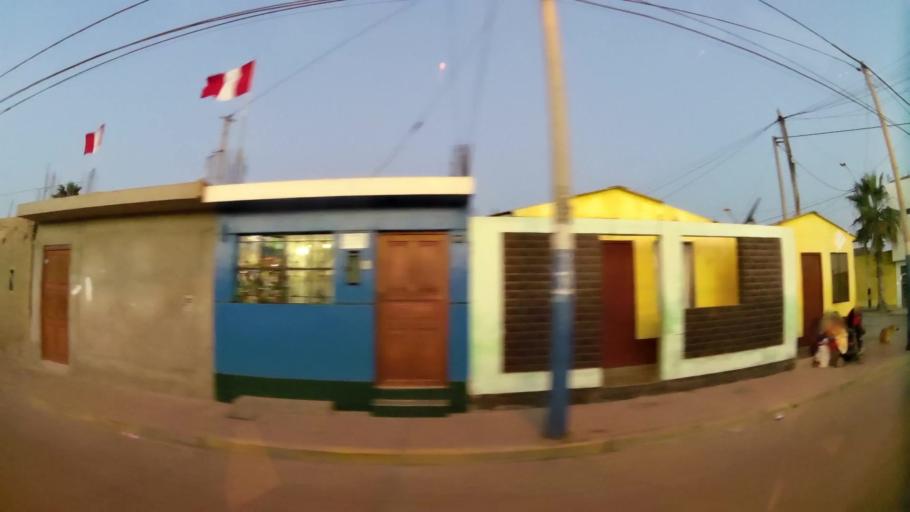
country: PE
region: Ica
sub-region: Provincia de Pisco
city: Pisco
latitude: -13.7141
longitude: -76.2190
